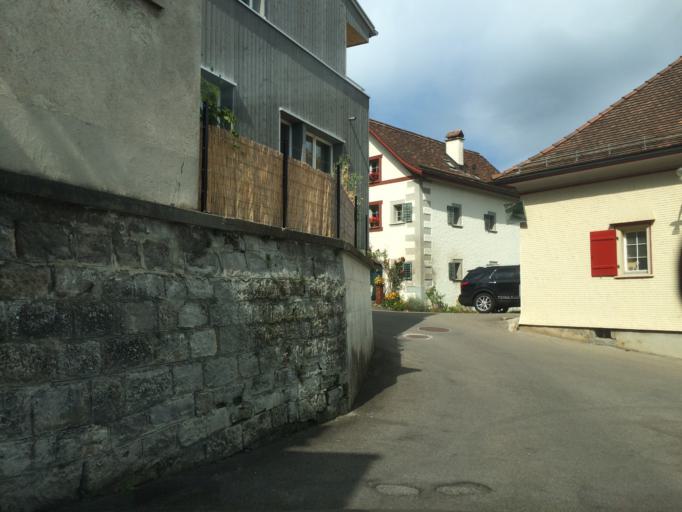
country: CH
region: Appenzell Ausserrhoden
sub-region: Bezirk Mittelland
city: Trogen
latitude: 47.4086
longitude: 9.4649
